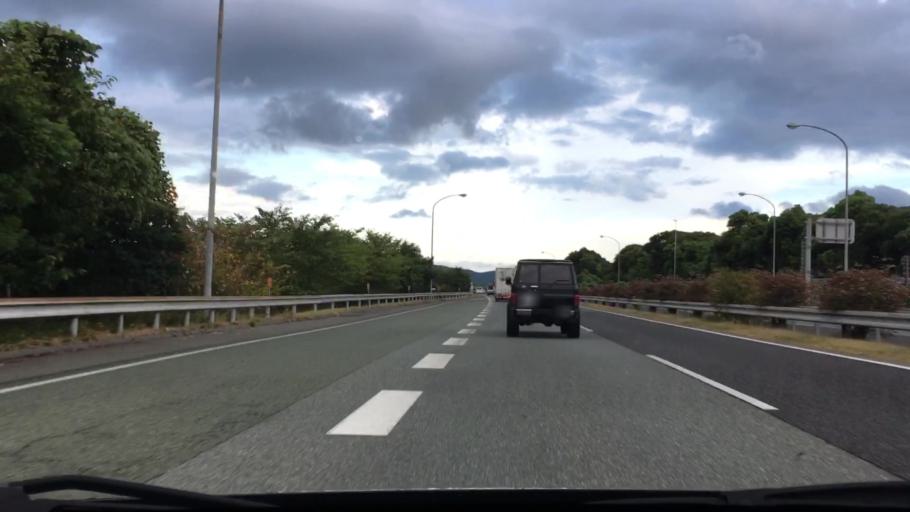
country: JP
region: Fukuoka
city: Kitakyushu
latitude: 33.8332
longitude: 130.9125
